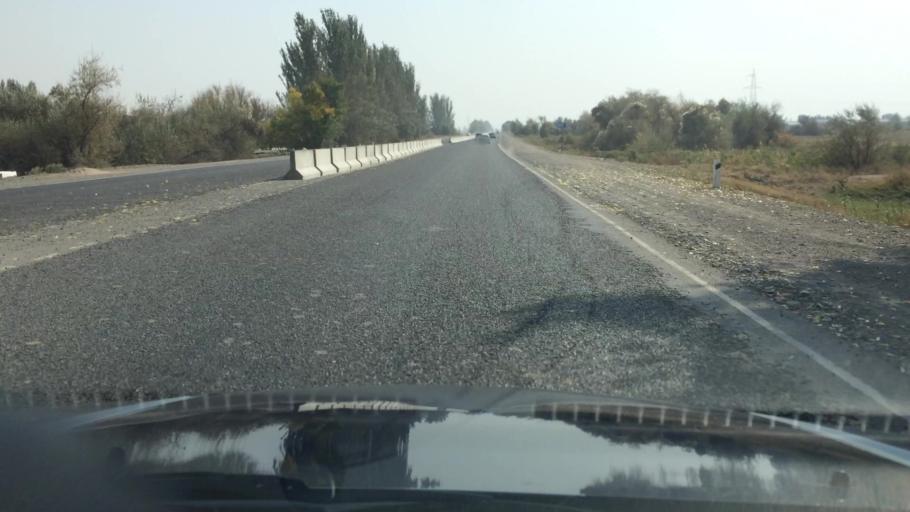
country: KG
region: Chuy
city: Kant
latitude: 42.9740
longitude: 74.8959
